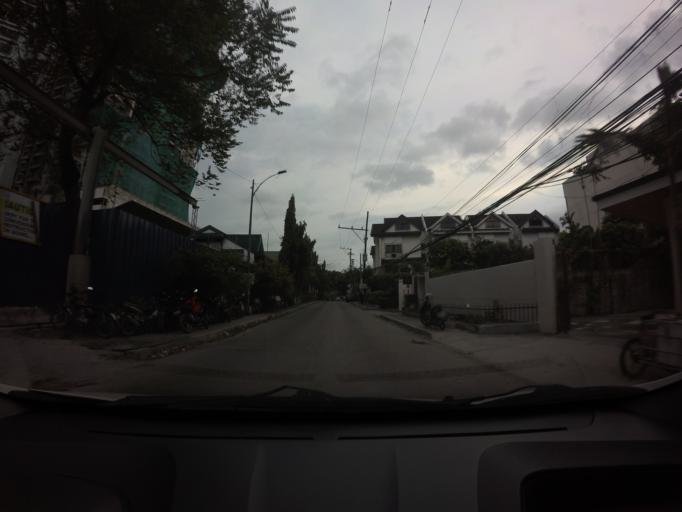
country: PH
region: Calabarzon
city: Del Monte
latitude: 14.6204
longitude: 121.0216
